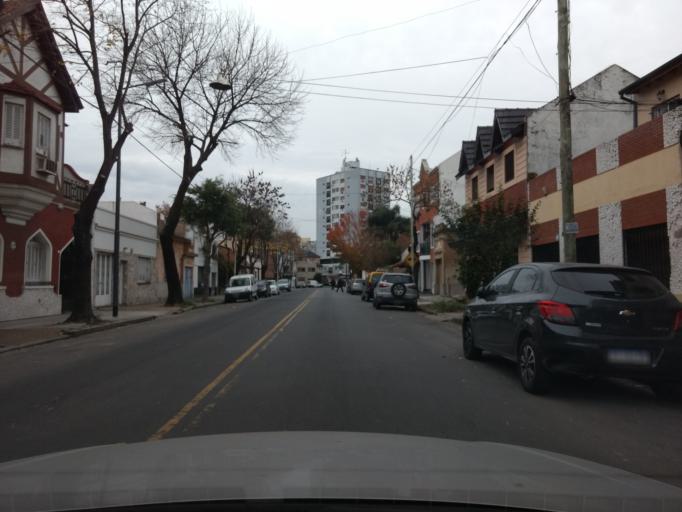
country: AR
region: Buenos Aires F.D.
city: Villa Santa Rita
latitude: -34.6340
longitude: -58.4910
